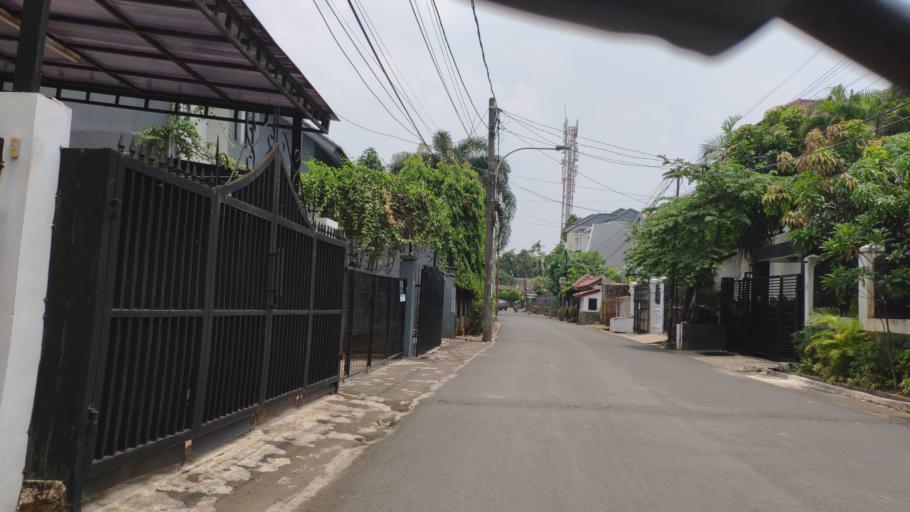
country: ID
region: Jakarta Raya
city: Jakarta
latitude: -6.2685
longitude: 106.7962
